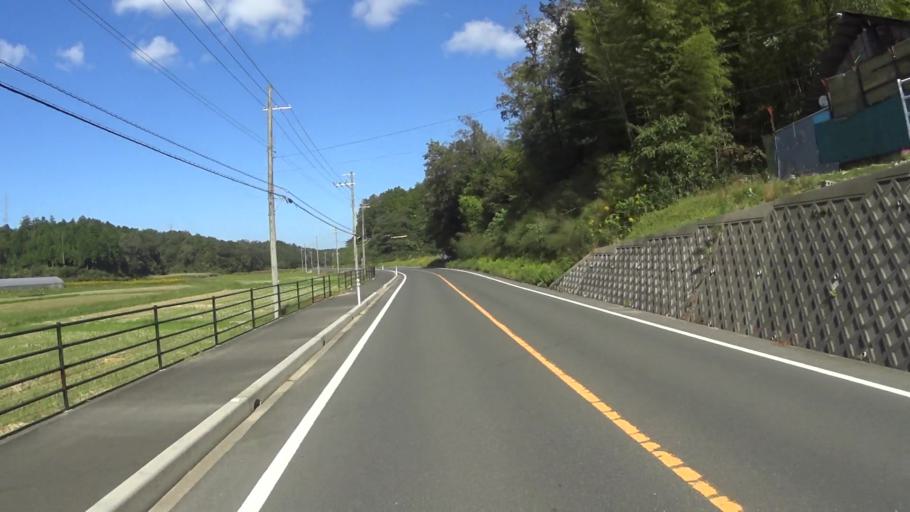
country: JP
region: Kyoto
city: Miyazu
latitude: 35.6421
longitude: 135.0722
